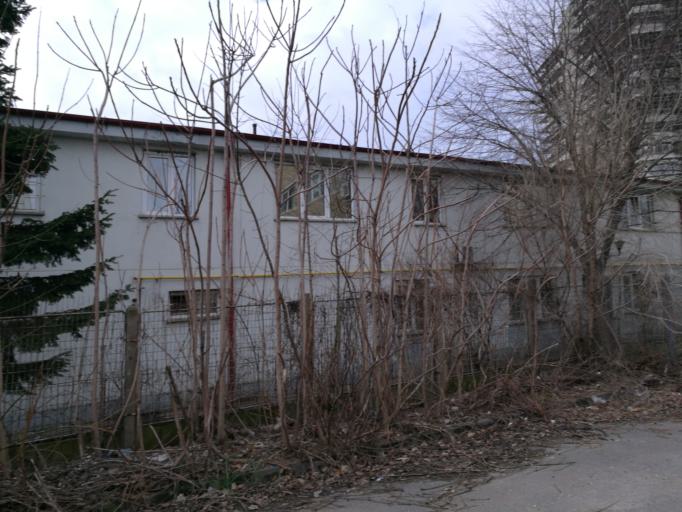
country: RO
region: Ilfov
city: Dobroesti
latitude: 44.4393
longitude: 26.1827
